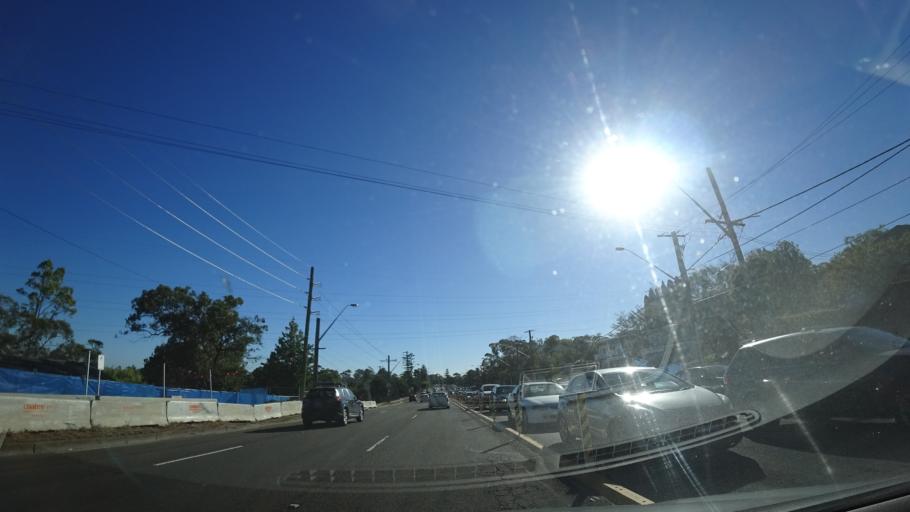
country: AU
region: New South Wales
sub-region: Warringah
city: Forestville
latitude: -33.7537
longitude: 151.2241
